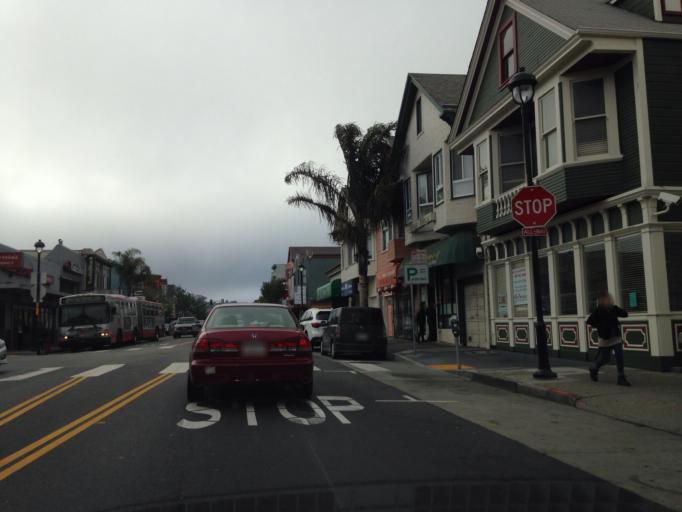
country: US
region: California
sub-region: San Francisco County
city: San Francisco
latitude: 37.7299
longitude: -122.4045
